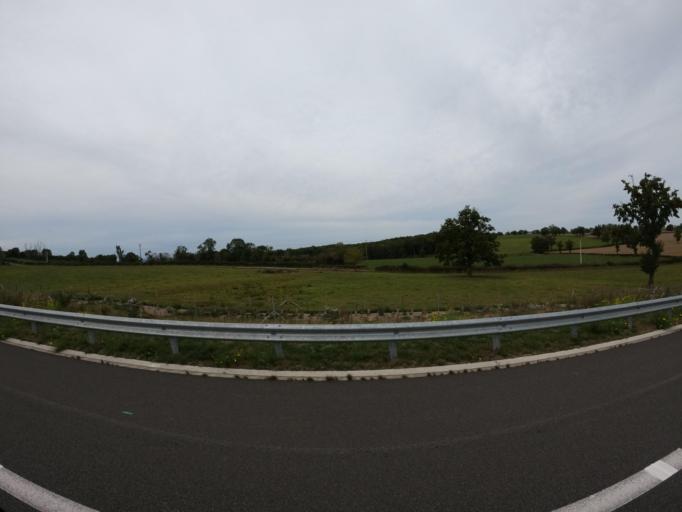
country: FR
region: Auvergne
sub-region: Departement de l'Allier
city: Montmarault
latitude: 46.3374
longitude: 2.9811
